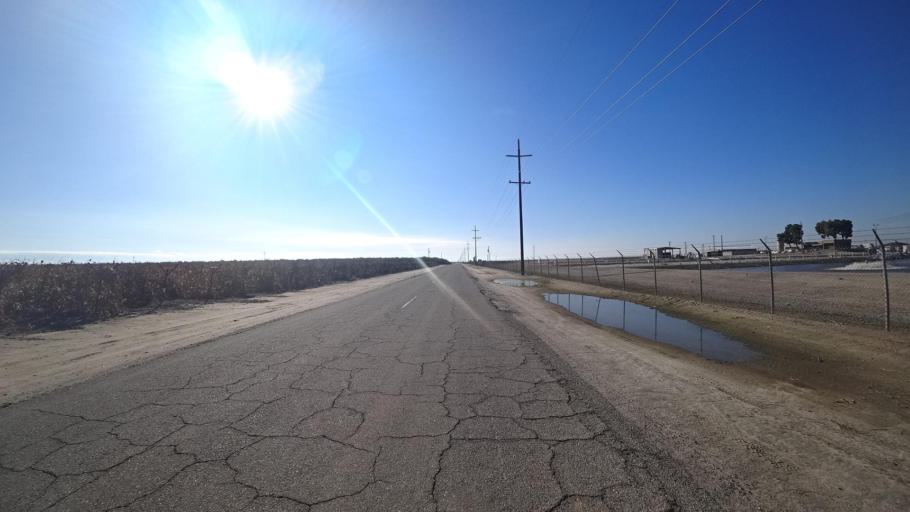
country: US
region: California
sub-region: Kern County
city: McFarland
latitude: 35.6838
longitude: -119.2766
